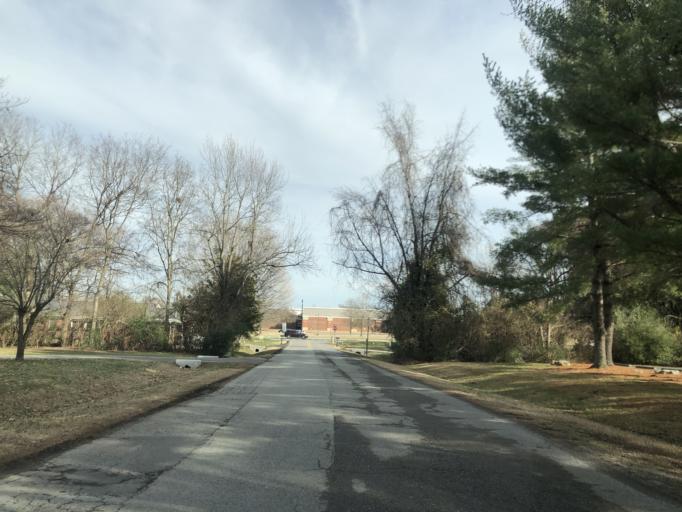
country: US
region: Tennessee
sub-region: Williamson County
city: Franklin
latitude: 35.9396
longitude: -86.8809
